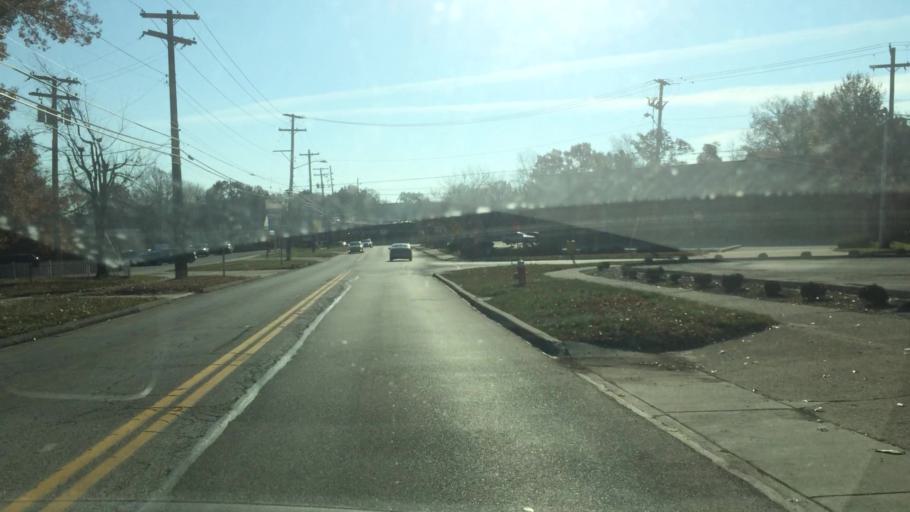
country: US
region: Ohio
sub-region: Summit County
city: Cuyahoga Falls
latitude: 41.1336
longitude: -81.4667
